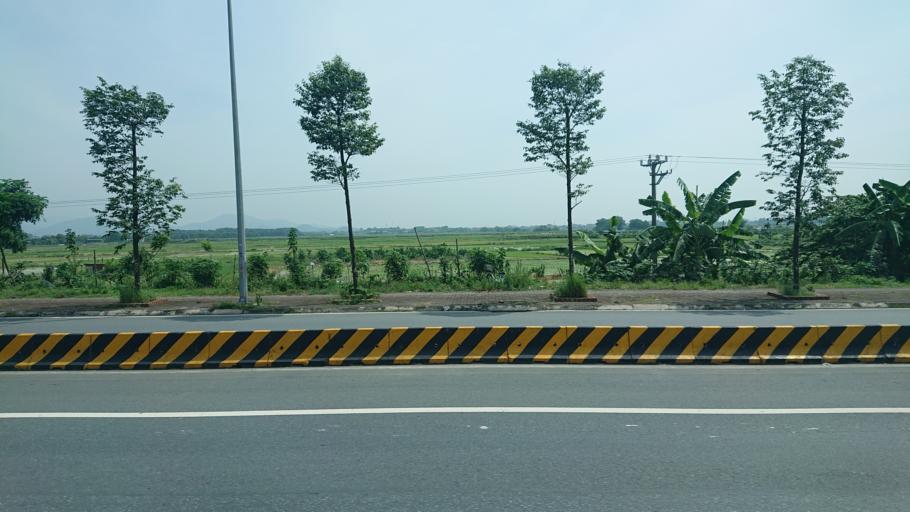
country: VN
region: Ha Noi
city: Soc Son
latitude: 21.2058
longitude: 105.8283
